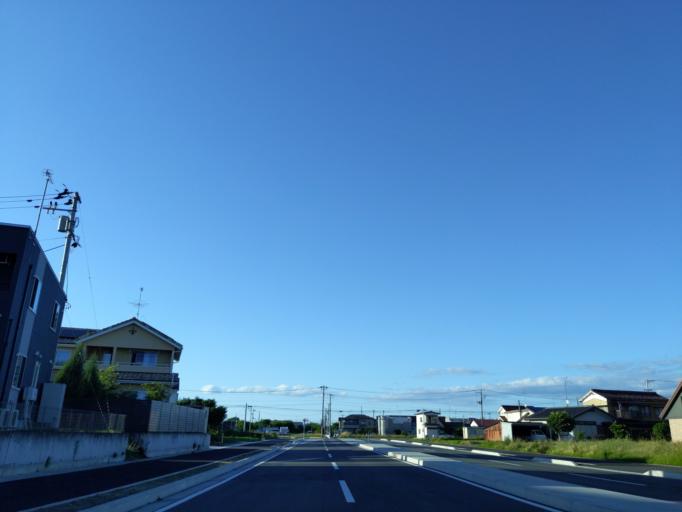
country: JP
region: Fukushima
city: Koriyama
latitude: 37.3922
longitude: 140.4016
